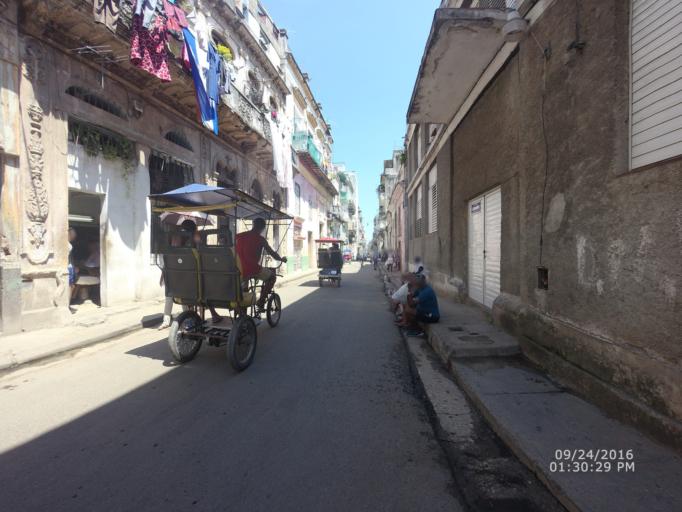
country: CU
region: La Habana
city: La Habana Vieja
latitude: 23.1332
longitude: -82.3554
